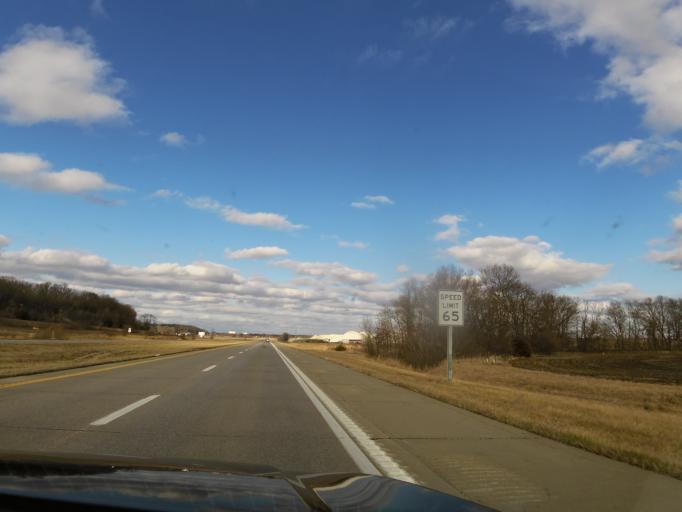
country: US
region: Missouri
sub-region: Clark County
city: Kahoka
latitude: 40.4317
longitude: -91.5700
